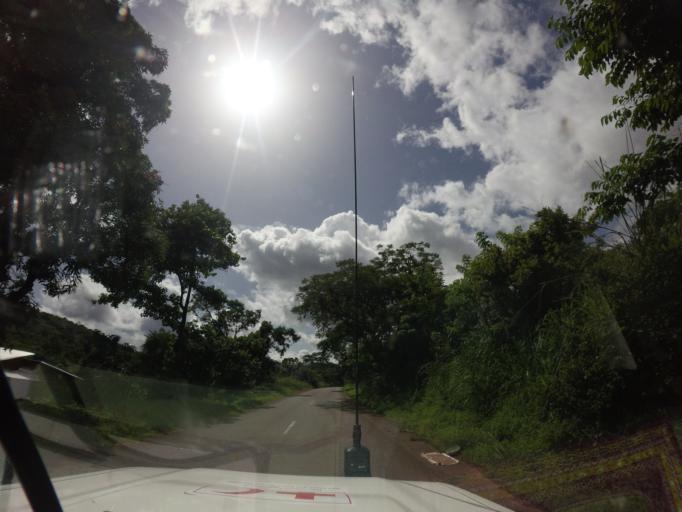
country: GN
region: Mamou
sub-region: Mamou Prefecture
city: Mamou
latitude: 10.3291
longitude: -12.0254
